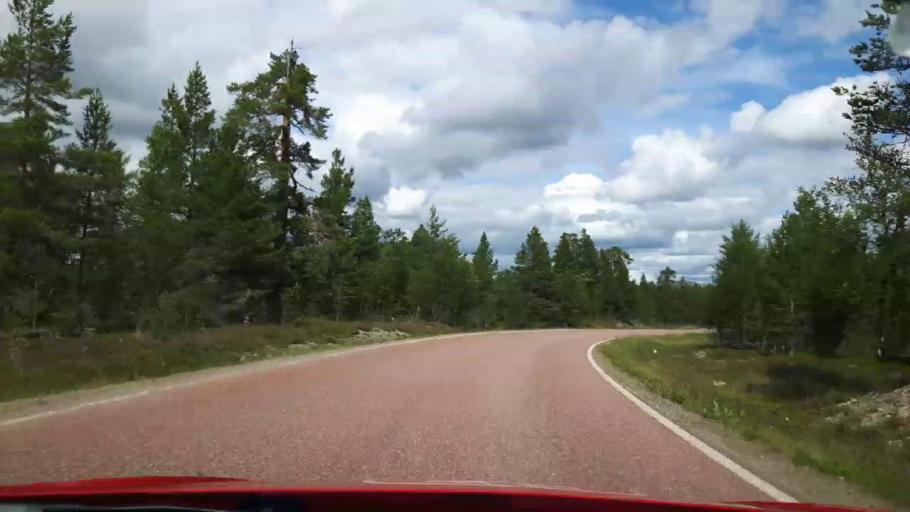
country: NO
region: Hedmark
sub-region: Trysil
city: Innbygda
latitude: 62.0963
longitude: 12.9725
